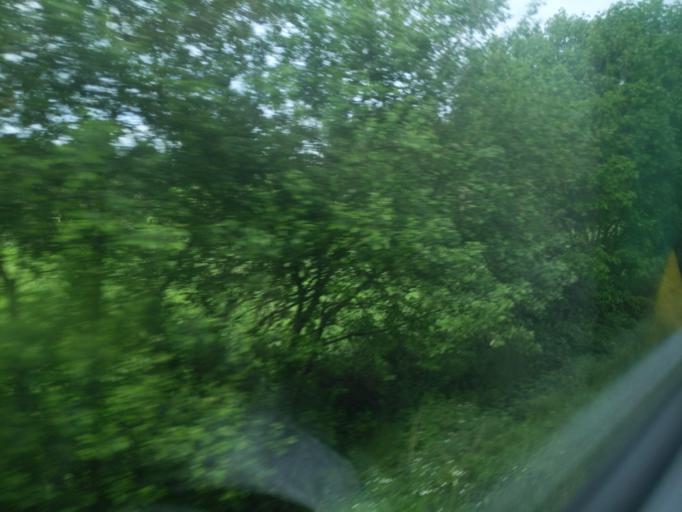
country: GB
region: England
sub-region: Devon
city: Crediton
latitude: 50.7810
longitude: -3.6041
